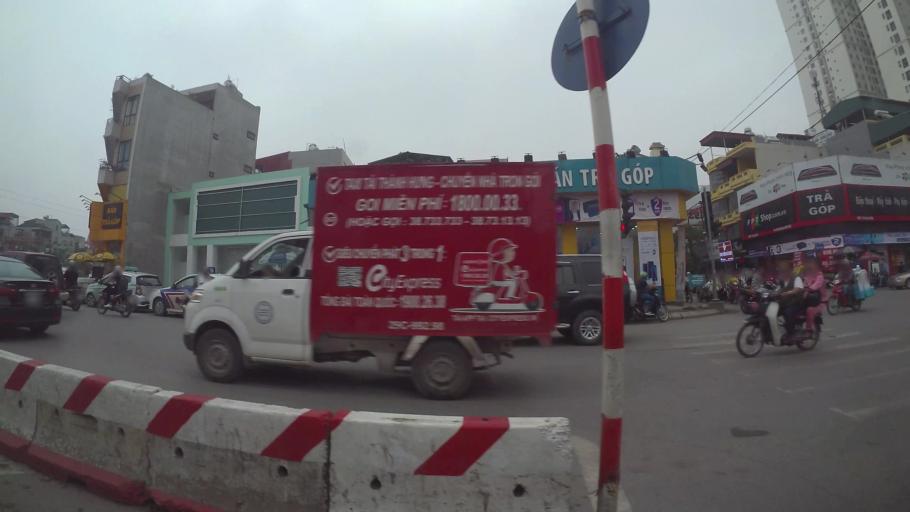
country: VN
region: Ha Noi
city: Hai BaTrung
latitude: 20.9837
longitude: 105.8459
